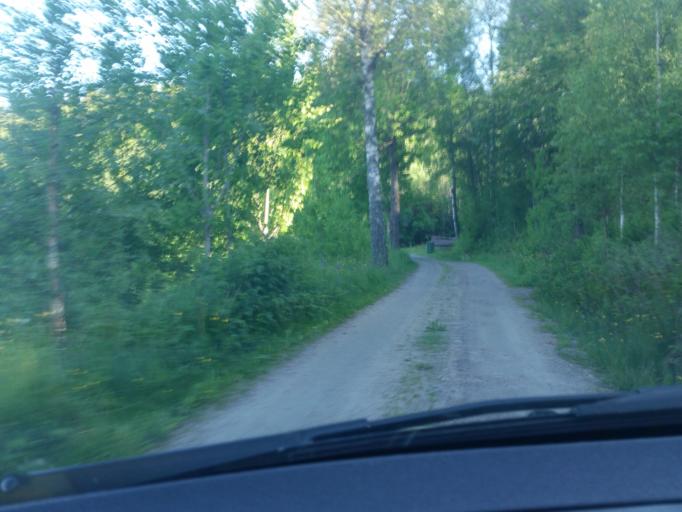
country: SE
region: Vaestra Goetaland
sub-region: Fargelanda Kommun
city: Faergelanda
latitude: 58.5874
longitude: 12.0300
